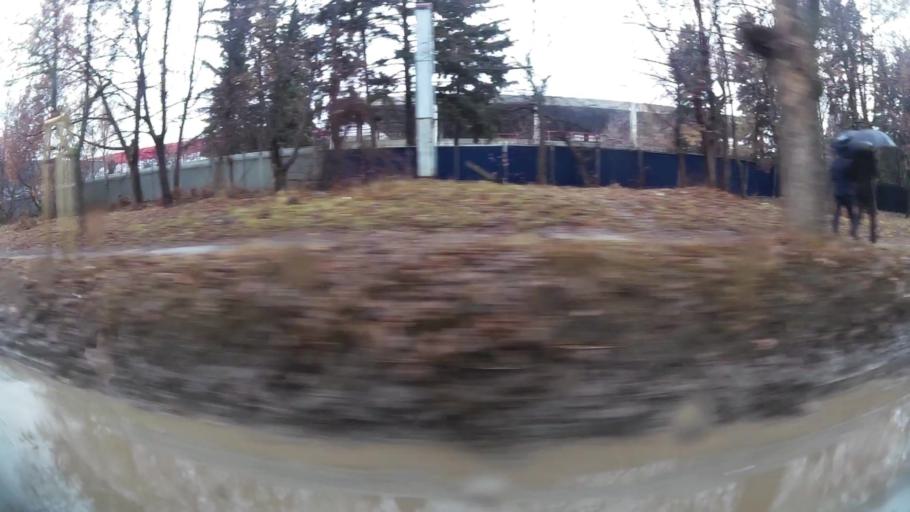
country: BG
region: Sofia-Capital
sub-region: Stolichna Obshtina
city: Sofia
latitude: 42.6369
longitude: 23.4073
